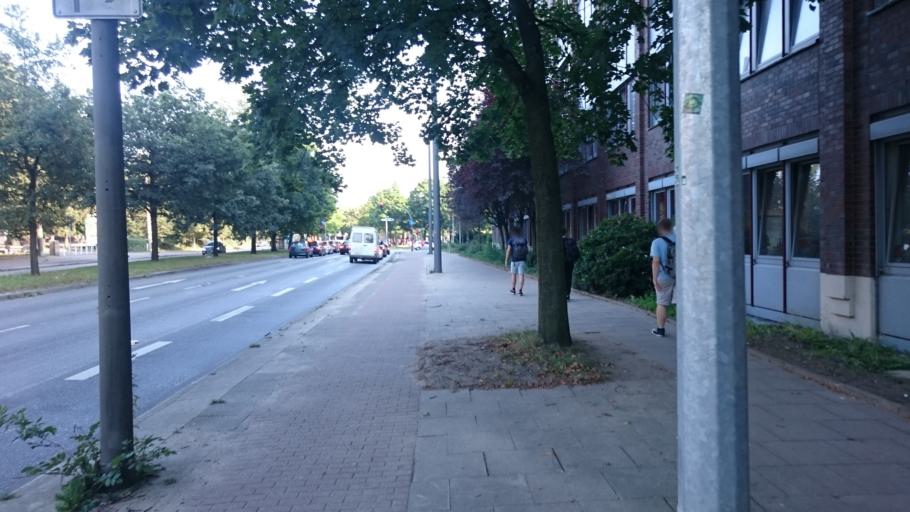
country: DE
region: Hamburg
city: Eidelstedt
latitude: 53.5747
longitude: 9.8905
